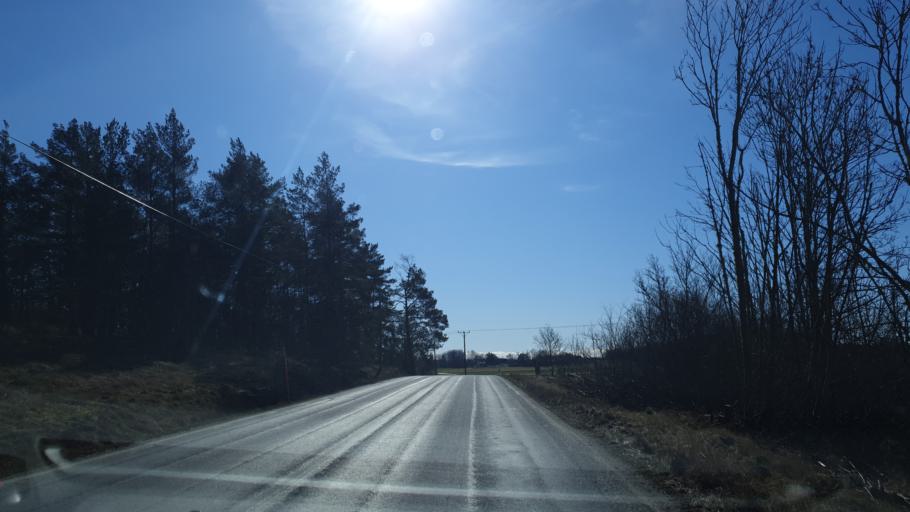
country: SE
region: Uppsala
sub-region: Enkopings Kommun
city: Grillby
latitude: 59.6055
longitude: 17.2748
